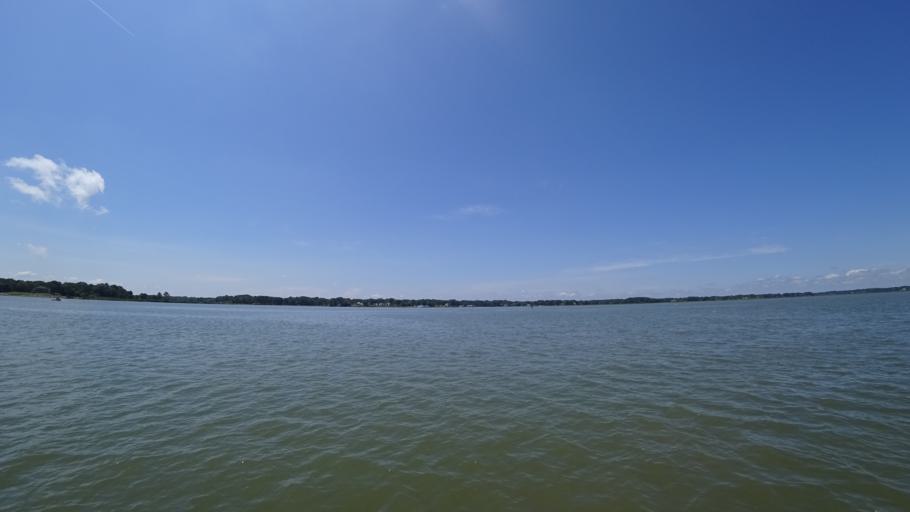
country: US
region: Virginia
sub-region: Isle of Wight County
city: Carrollton
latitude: 37.0085
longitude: -76.5727
